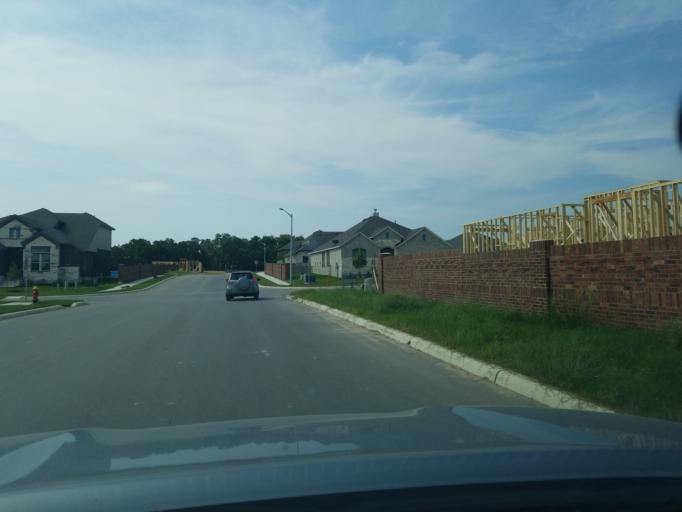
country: US
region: Texas
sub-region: Kendall County
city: Boerne
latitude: 29.7542
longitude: -98.7143
